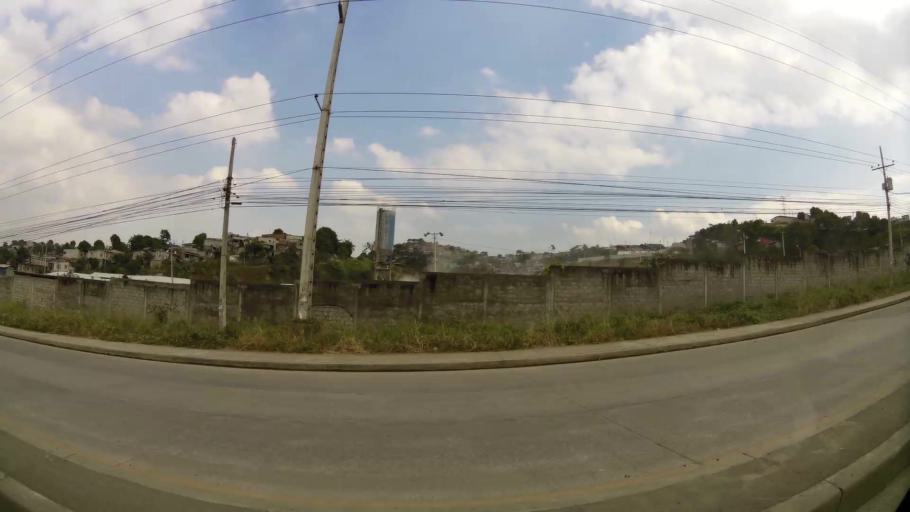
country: EC
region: Guayas
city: Santa Lucia
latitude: -2.1187
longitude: -79.9611
